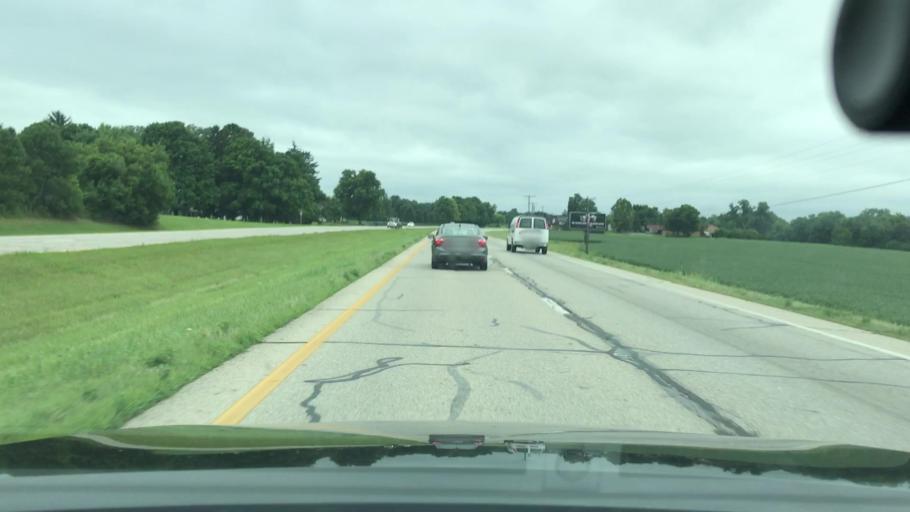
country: US
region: Ohio
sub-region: Pickaway County
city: Logan Elm Village
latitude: 39.5055
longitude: -82.9739
